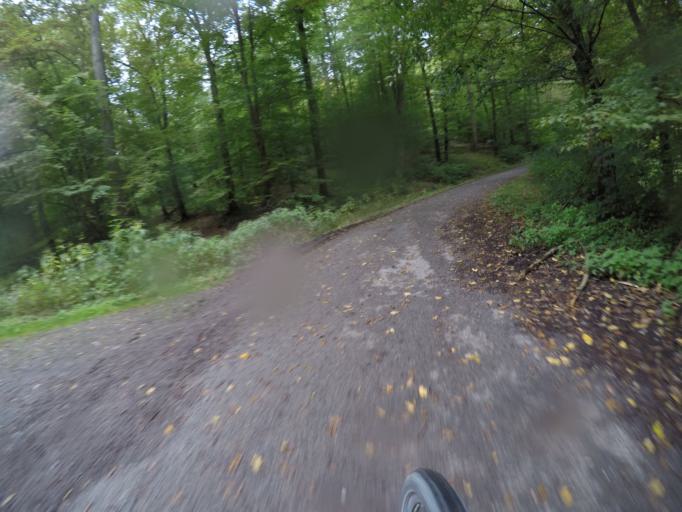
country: DE
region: Baden-Wuerttemberg
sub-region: Regierungsbezirk Stuttgart
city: Gerlingen
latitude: 48.7643
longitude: 9.0463
